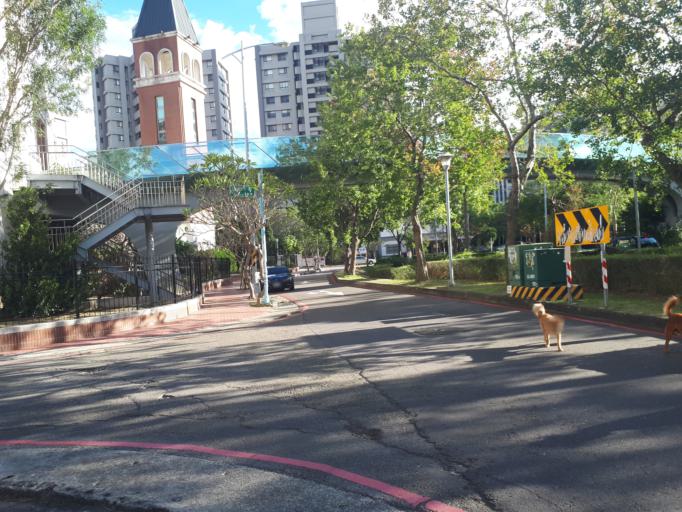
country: TW
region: Taiwan
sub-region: Hsinchu
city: Zhubei
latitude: 24.8055
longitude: 121.0354
